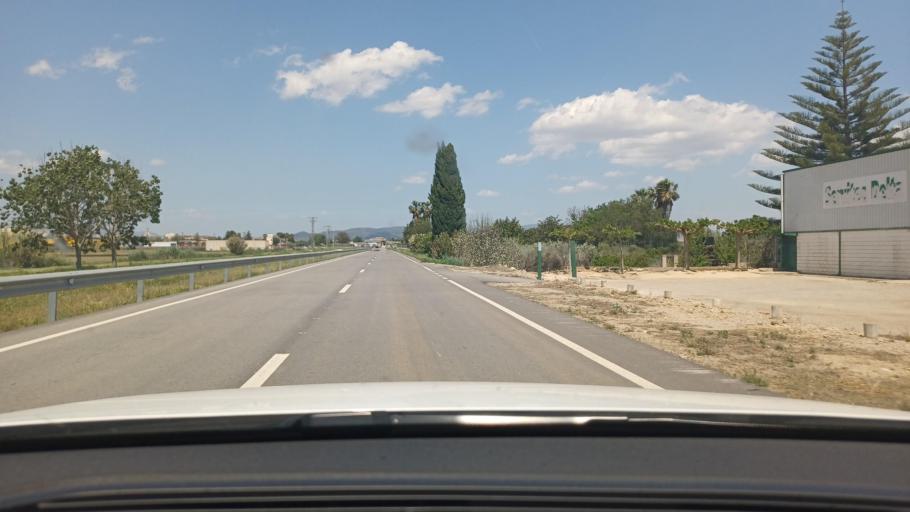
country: ES
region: Catalonia
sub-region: Provincia de Tarragona
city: Amposta
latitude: 40.6974
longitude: 0.5891
